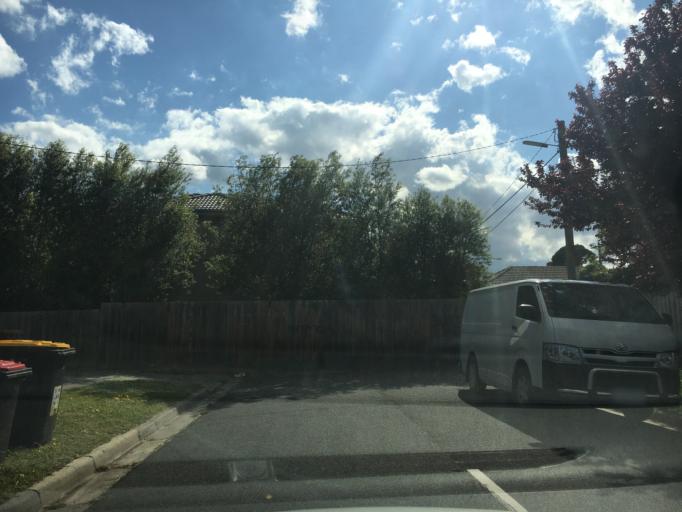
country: AU
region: Victoria
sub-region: Monash
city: Clayton
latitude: -37.9225
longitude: 145.1299
